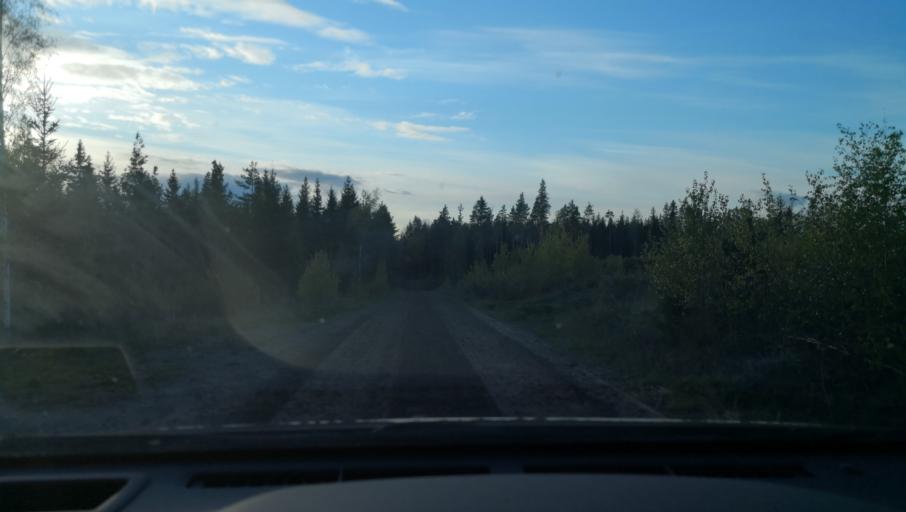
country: SE
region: OErebro
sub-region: Askersunds Kommun
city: Asbro
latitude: 58.8835
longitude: 15.1291
